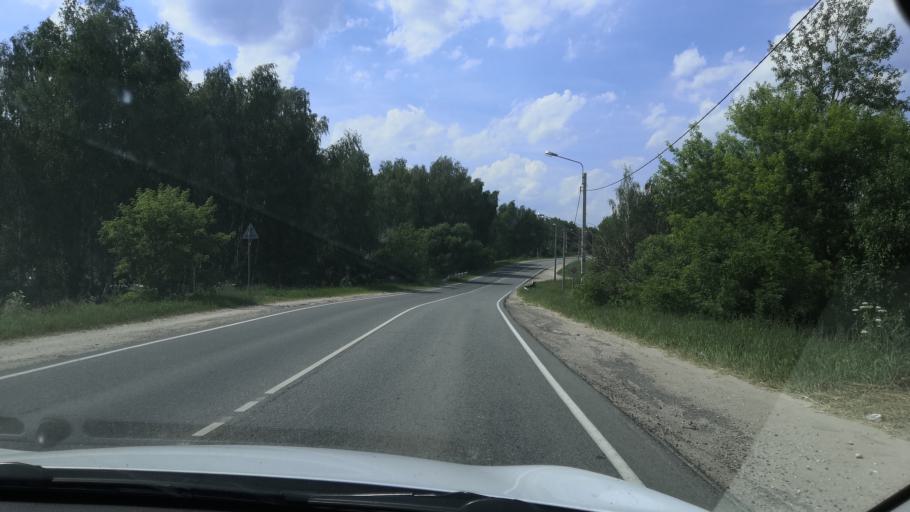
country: RU
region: Rjazan
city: Murmino
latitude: 54.5939
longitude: 40.0945
